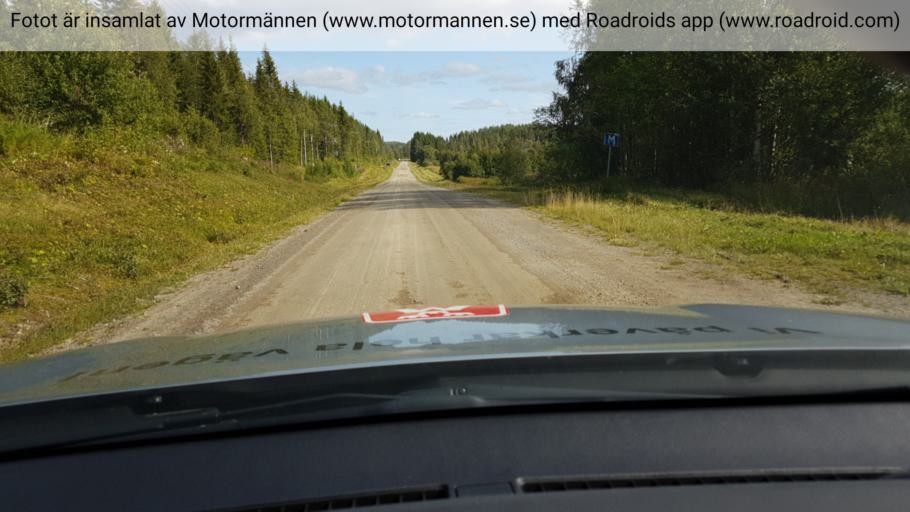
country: SE
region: Jaemtland
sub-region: Ragunda Kommun
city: Hammarstrand
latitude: 63.4887
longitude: 16.0735
